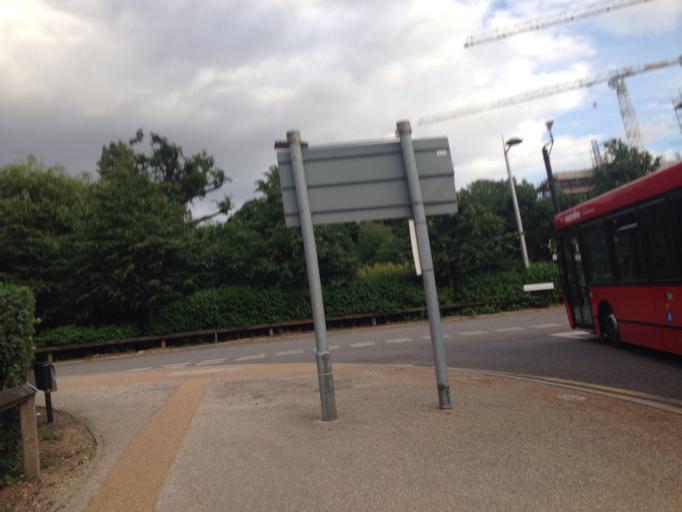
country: GB
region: England
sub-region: Greater London
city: Ealing Broadway
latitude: 51.5322
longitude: -0.2857
